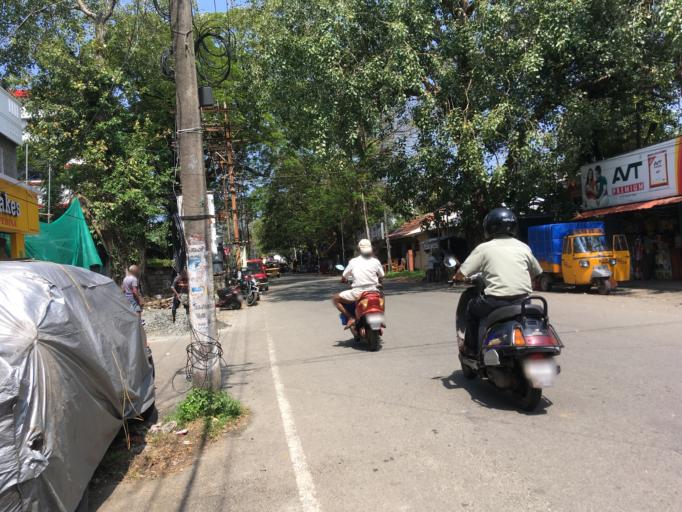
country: IN
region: Kerala
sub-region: Ernakulam
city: Cochin
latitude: 9.9585
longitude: 76.2452
